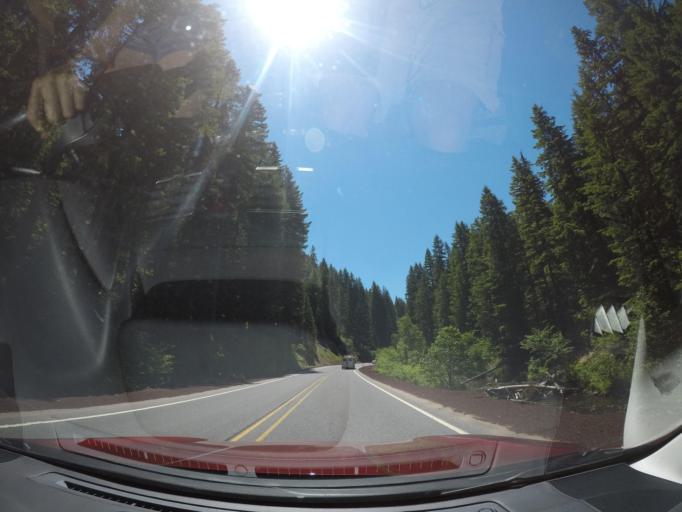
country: US
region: Oregon
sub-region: Deschutes County
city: Sisters
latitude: 44.5478
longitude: -121.9943
